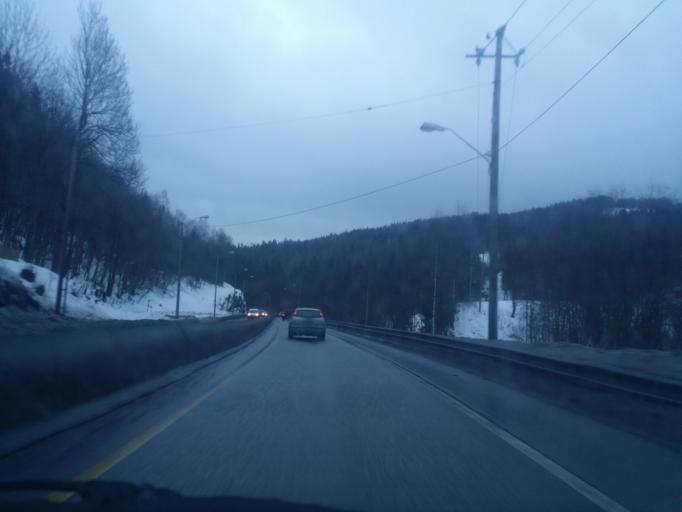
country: NO
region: Akershus
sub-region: Baerum
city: Skui
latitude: 59.9396
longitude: 10.4070
